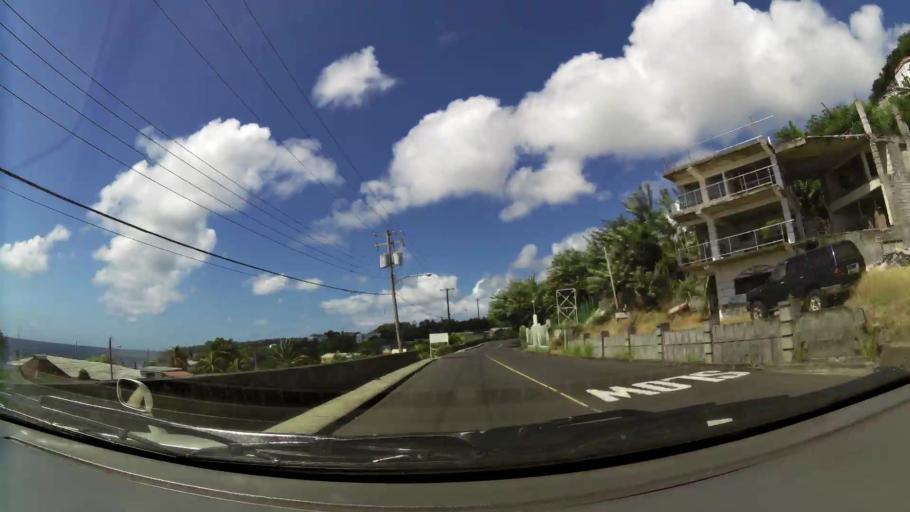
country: VC
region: Saint George
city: Kingstown
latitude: 13.1336
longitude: -61.2003
